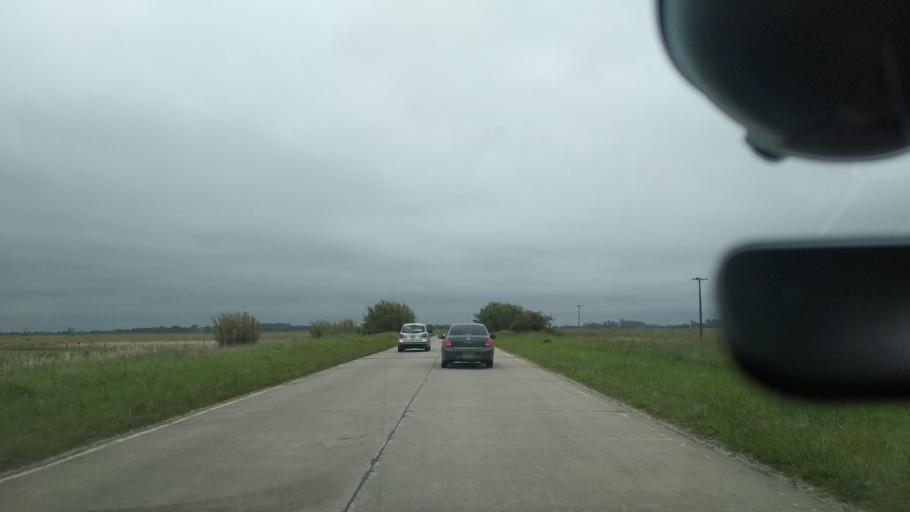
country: AR
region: Buenos Aires
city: Veronica
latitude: -35.5559
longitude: -57.3057
